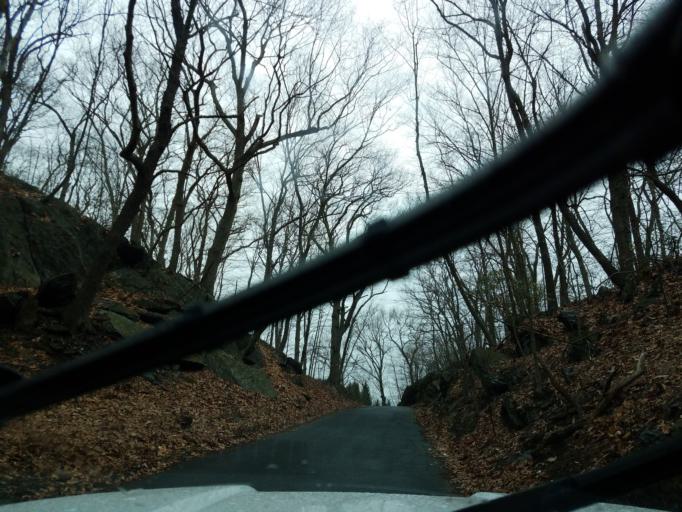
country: US
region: Connecticut
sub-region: Fairfield County
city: Shelton
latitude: 41.3056
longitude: -73.0816
